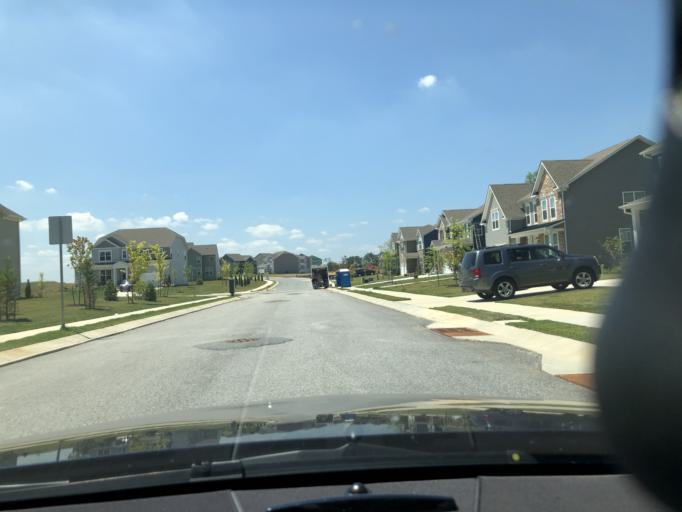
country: US
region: Maryland
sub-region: Carroll County
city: Westminster
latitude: 39.5584
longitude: -76.9743
